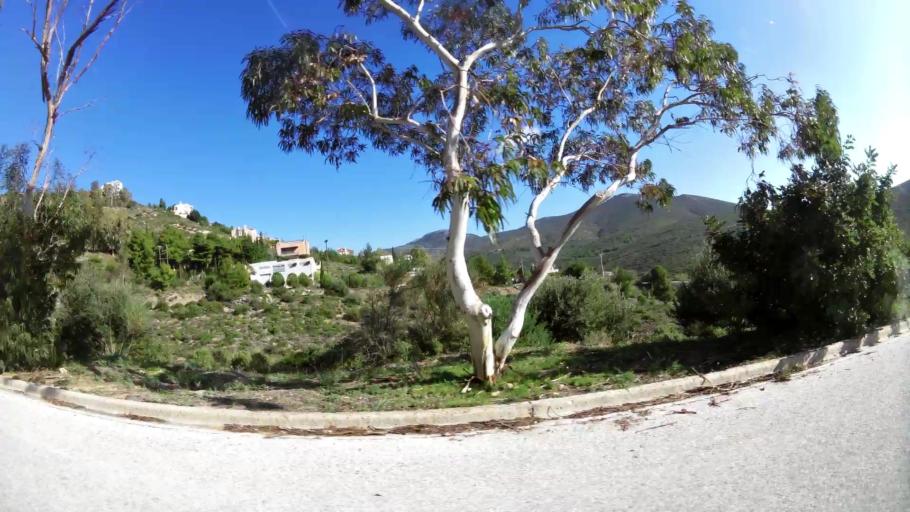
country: GR
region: Attica
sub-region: Nomarchia Anatolikis Attikis
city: Dhrafi
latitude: 38.0387
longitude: 23.9030
